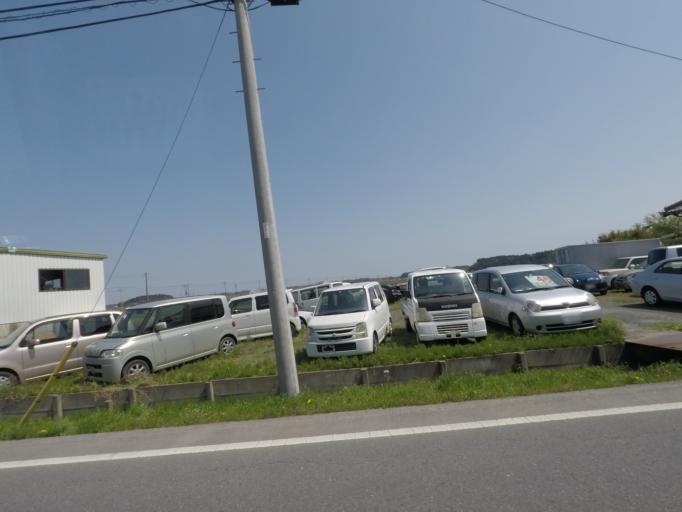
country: JP
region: Chiba
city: Yokaichiba
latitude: 35.7009
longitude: 140.4556
